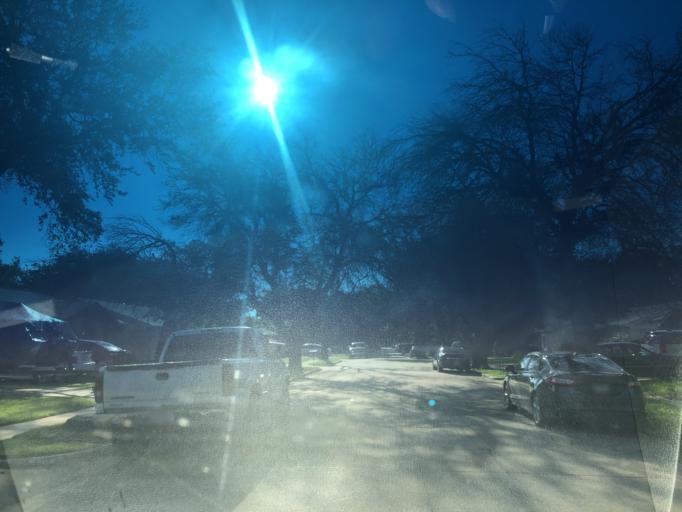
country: US
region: Texas
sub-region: Dallas County
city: Grand Prairie
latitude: 32.6983
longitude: -97.0011
